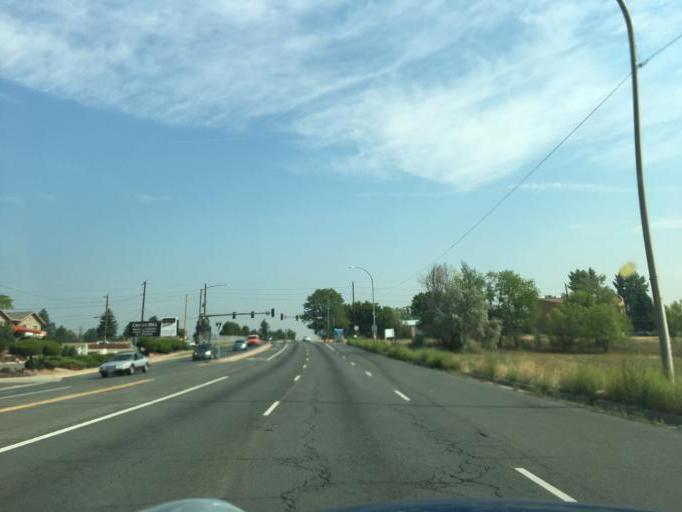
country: US
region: Colorado
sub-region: Jefferson County
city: Wheat Ridge
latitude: 39.7534
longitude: -105.0813
